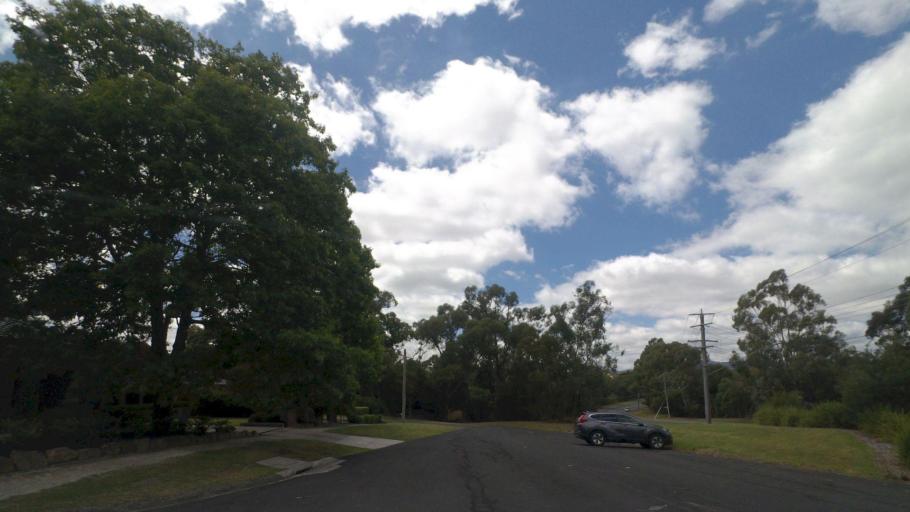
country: AU
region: Victoria
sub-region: Maroondah
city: Croydon Hills
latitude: -37.7686
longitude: 145.2737
